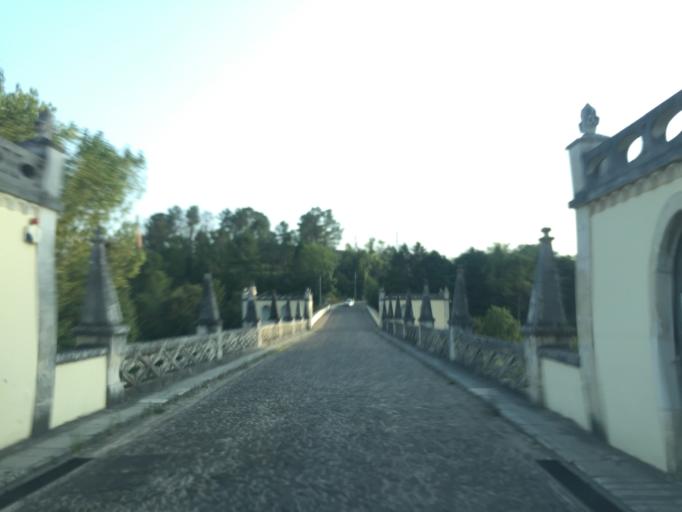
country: PT
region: Leiria
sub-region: Batalha
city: Batalha
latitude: 39.6584
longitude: -8.8308
